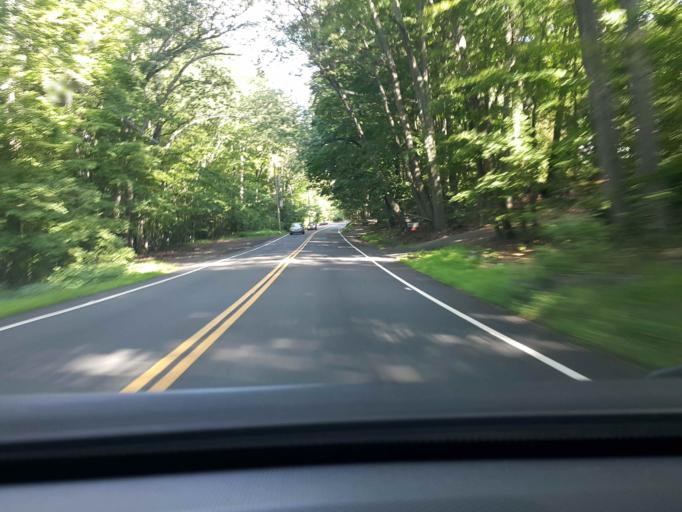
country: US
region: Connecticut
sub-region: New Haven County
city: Guilford
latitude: 41.3208
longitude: -72.6997
